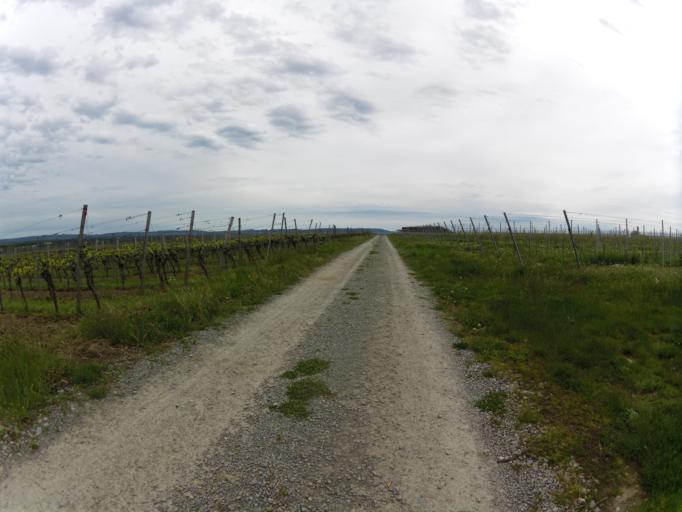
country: DE
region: Bavaria
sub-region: Regierungsbezirk Unterfranken
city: Sommerach
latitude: 49.8469
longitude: 10.1990
